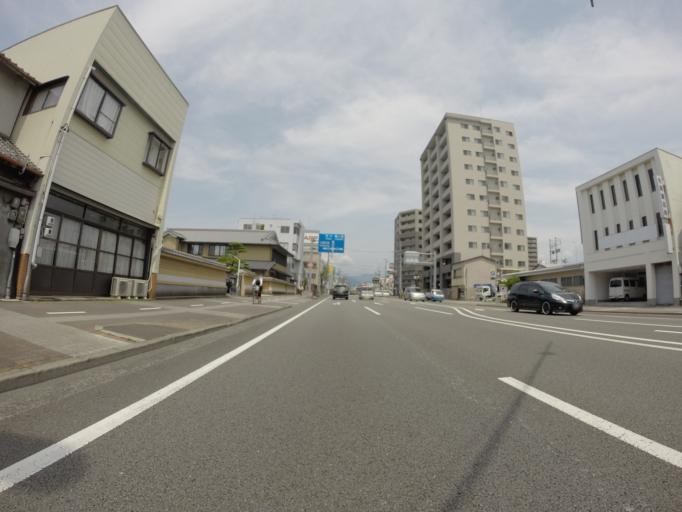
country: JP
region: Shizuoka
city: Shizuoka-shi
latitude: 34.9800
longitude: 138.3759
